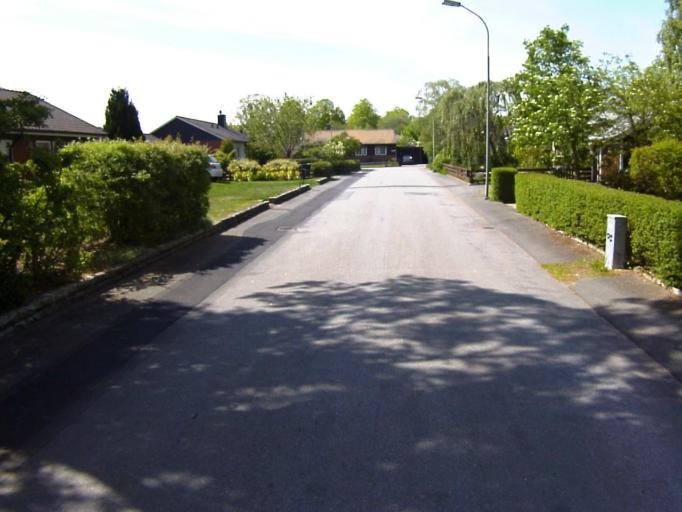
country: SE
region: Skane
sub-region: Kristianstads Kommun
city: Kristianstad
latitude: 56.0722
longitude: 14.0927
